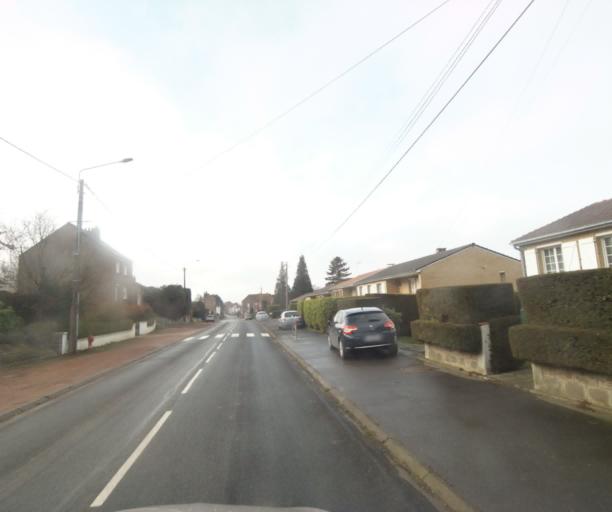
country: FR
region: Nord-Pas-de-Calais
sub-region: Departement du Nord
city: Maing
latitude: 50.3084
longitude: 3.4922
